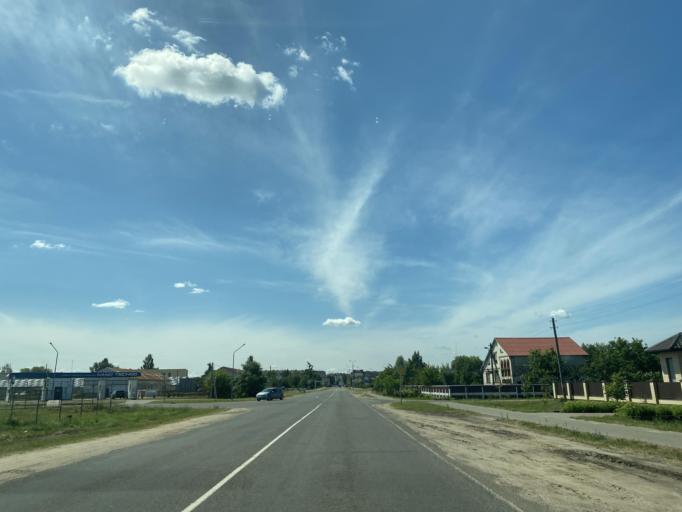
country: BY
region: Brest
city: Ivanava
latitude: 52.1561
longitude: 25.5445
